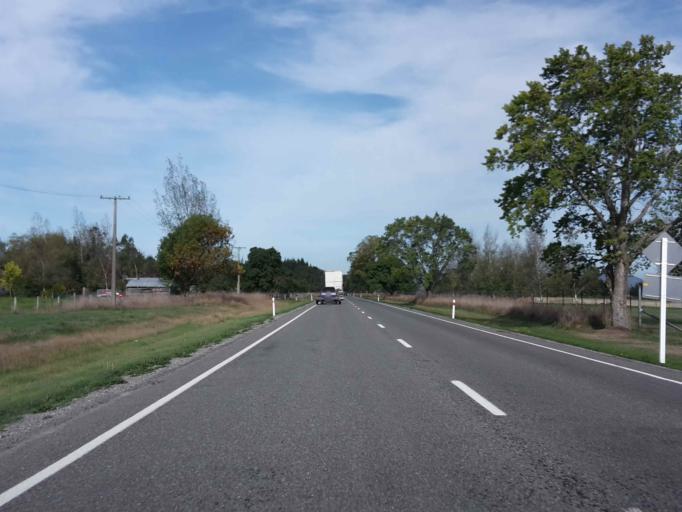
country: NZ
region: Canterbury
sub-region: Timaru District
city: Pleasant Point
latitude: -44.0749
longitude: 170.7971
